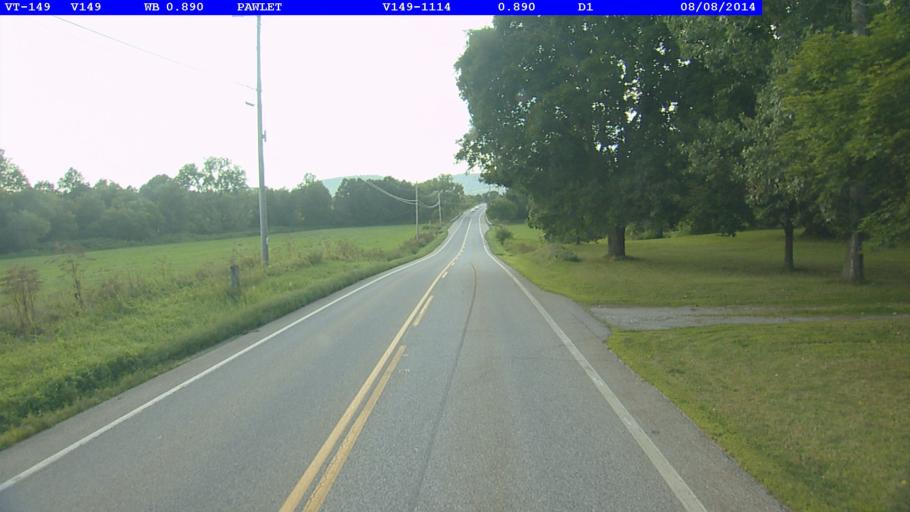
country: US
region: New York
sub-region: Washington County
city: Granville
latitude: 43.4026
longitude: -73.2341
